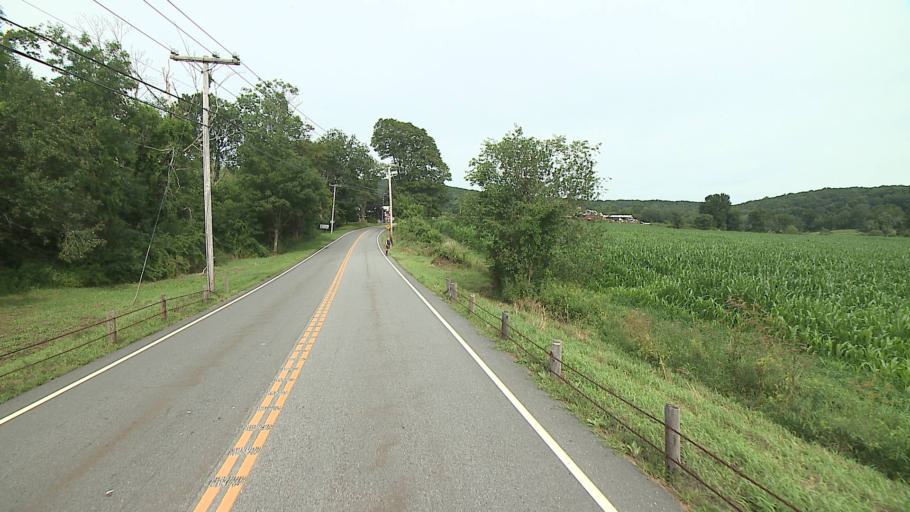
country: US
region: Connecticut
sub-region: Litchfield County
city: New Preston
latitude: 41.7198
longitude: -73.3319
